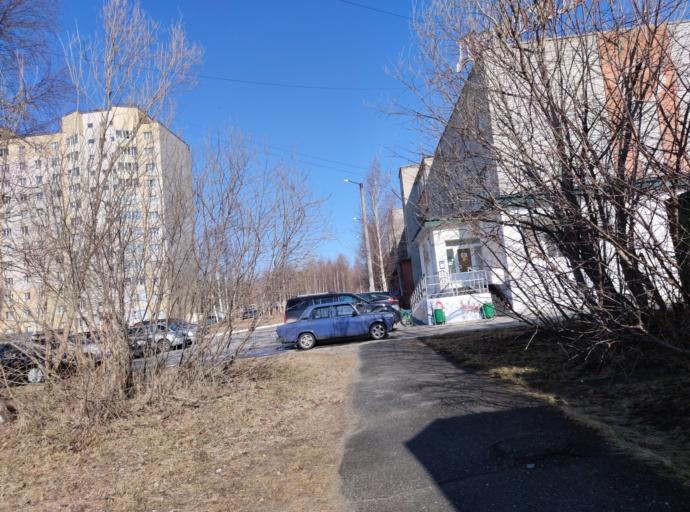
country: RU
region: Khanty-Mansiyskiy Avtonomnyy Okrug
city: Langepas
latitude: 61.2510
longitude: 75.1672
